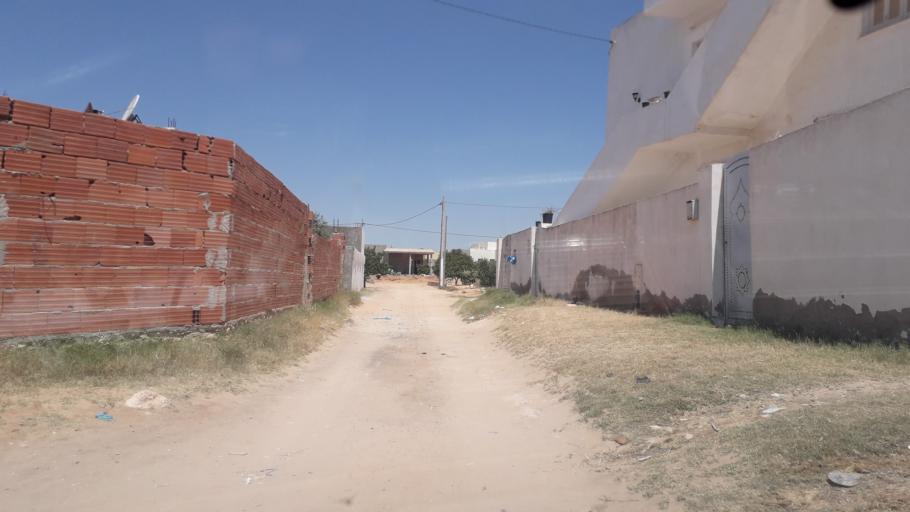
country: TN
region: Safaqis
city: Al Qarmadah
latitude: 34.8298
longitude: 10.7734
